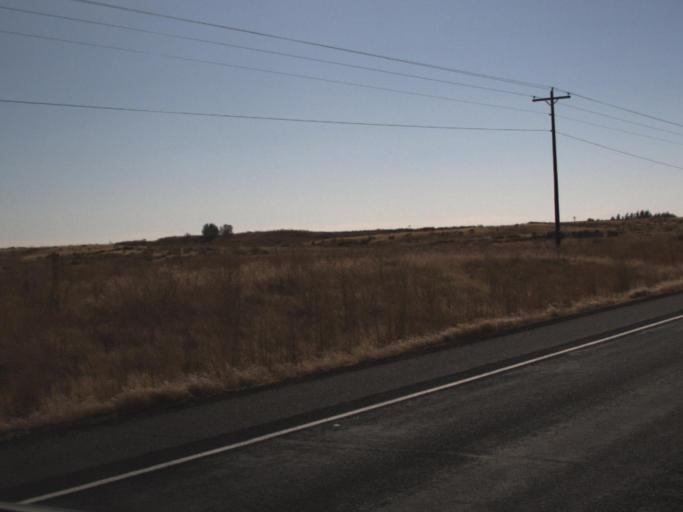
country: US
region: Washington
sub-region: Franklin County
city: Basin City
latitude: 46.6251
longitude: -119.0062
